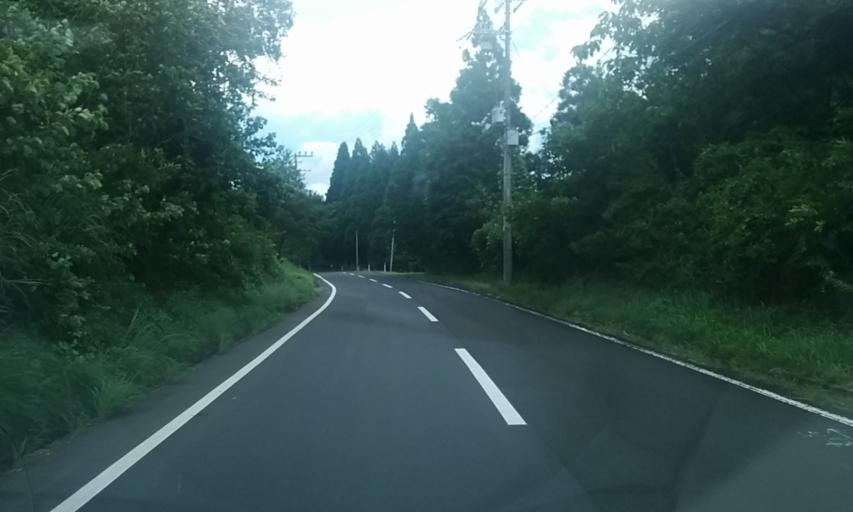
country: JP
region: Kyoto
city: Ayabe
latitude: 35.2845
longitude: 135.3318
